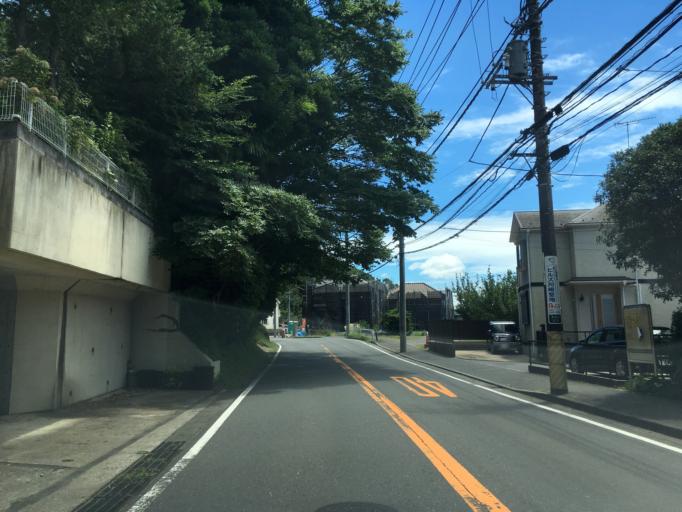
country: JP
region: Tokyo
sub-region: Machida-shi
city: Machida
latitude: 35.5584
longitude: 139.4875
